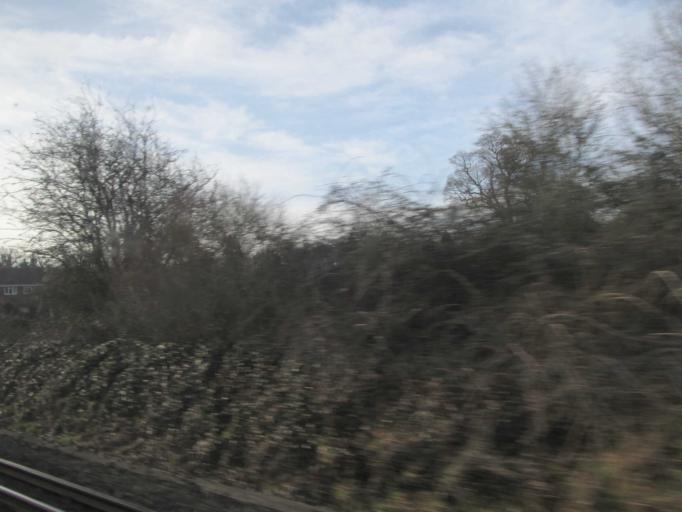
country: GB
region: England
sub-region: Wokingham
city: Winnersh
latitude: 51.4248
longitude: -0.8646
